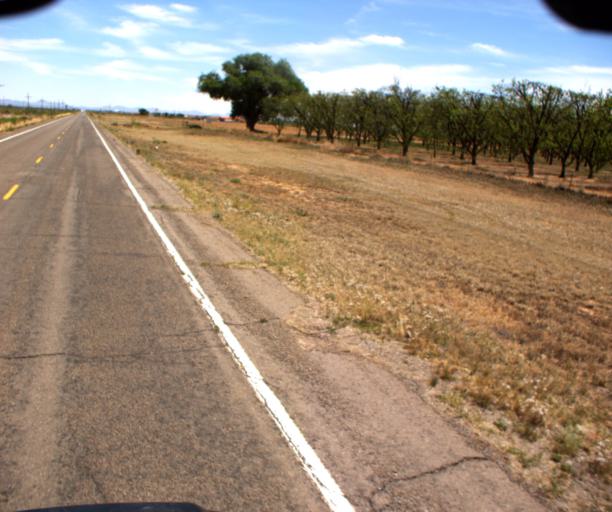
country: US
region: Arizona
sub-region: Cochise County
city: Willcox
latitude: 32.3235
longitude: -109.4668
